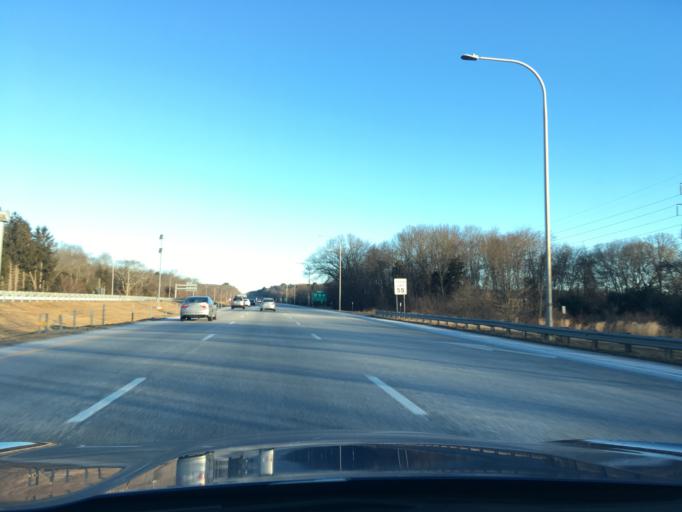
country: US
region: Rhode Island
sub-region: Kent County
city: East Greenwich
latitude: 41.6331
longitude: -71.4869
